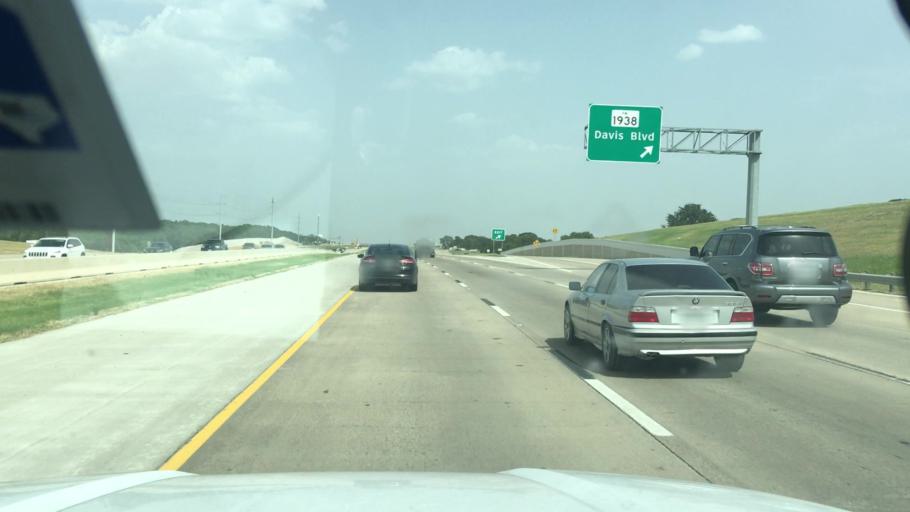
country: US
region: Texas
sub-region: Denton County
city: Trophy Club
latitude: 32.9921
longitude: -97.1914
